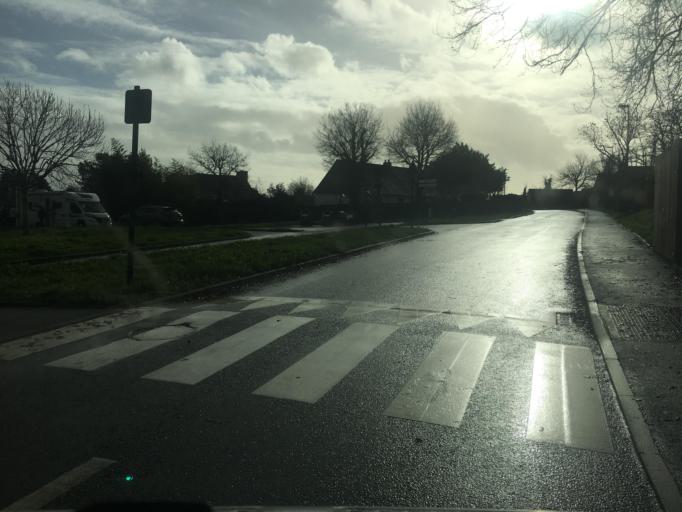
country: FR
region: Brittany
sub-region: Departement du Morbihan
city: Sarzeau
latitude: 47.5025
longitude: -2.7717
